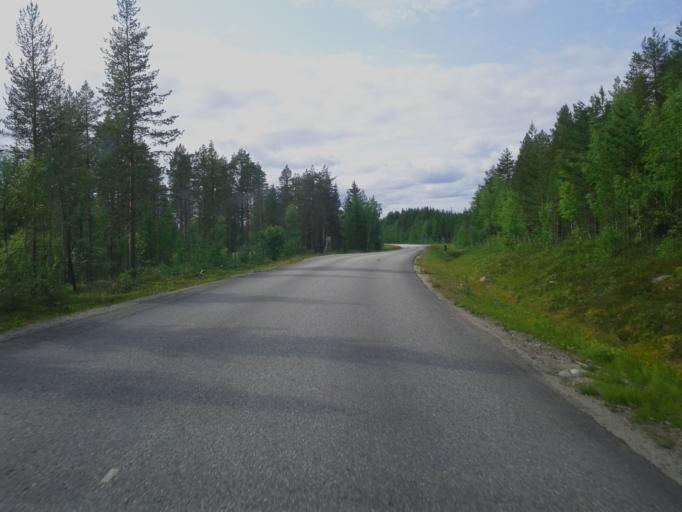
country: SE
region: Vaesterbotten
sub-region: Lycksele Kommun
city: Soderfors
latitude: 65.2758
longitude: 17.9472
